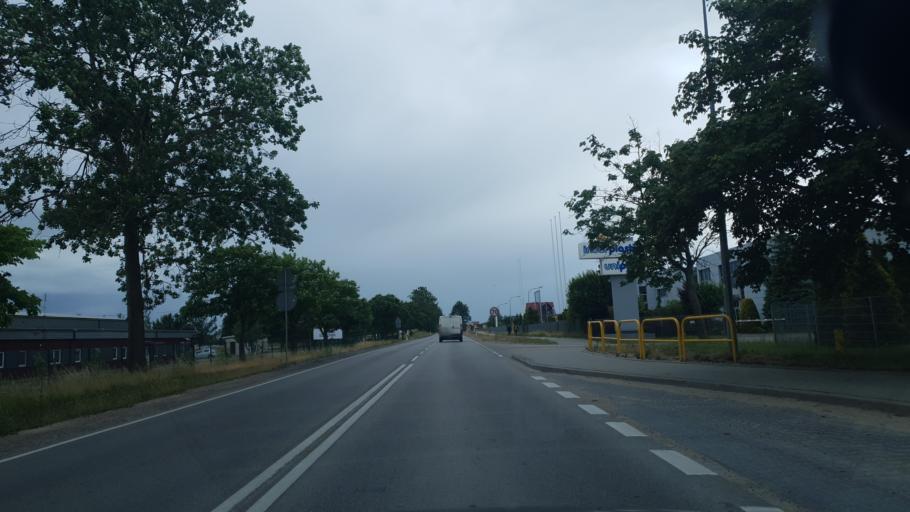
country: PL
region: Pomeranian Voivodeship
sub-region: Powiat kartuski
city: Banino
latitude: 54.4216
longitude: 18.3814
